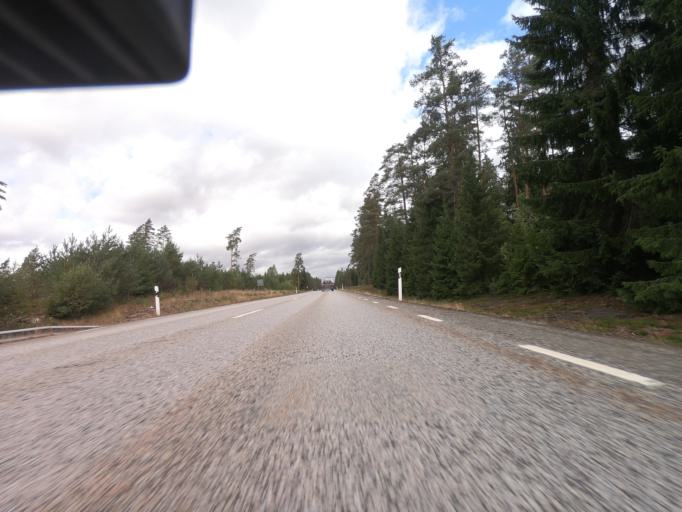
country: SE
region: Joenkoeping
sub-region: Vaggeryds Kommun
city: Vaggeryd
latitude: 57.5761
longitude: 14.2343
